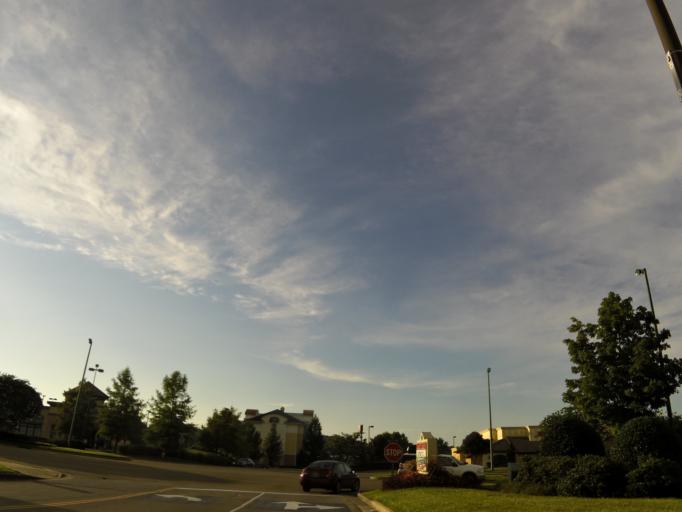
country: US
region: Tennessee
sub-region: Knox County
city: Farragut
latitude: 35.9023
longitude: -84.1497
